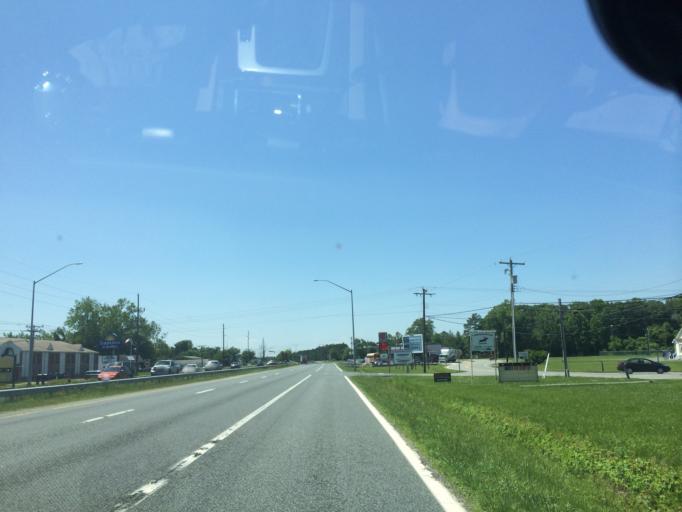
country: US
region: Maryland
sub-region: Dorchester County
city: Cambridge
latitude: 38.5529
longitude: -76.0393
